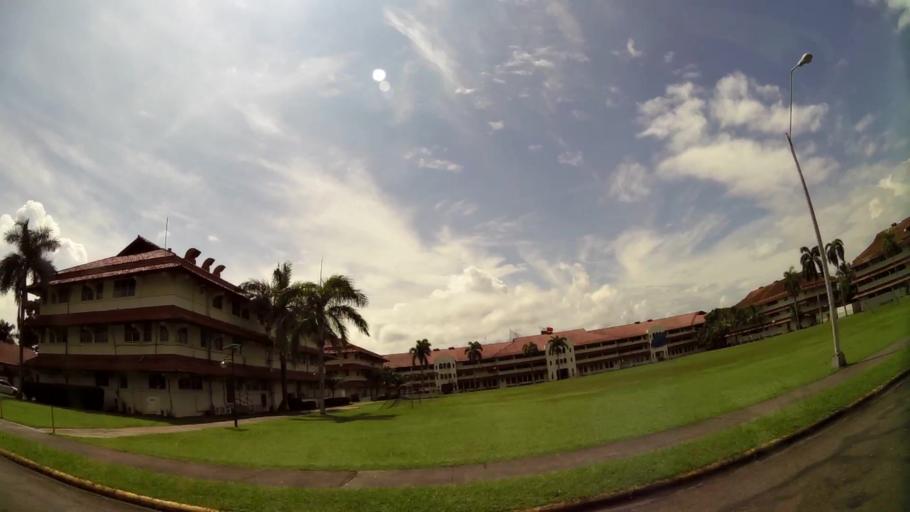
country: PA
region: Panama
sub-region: Distrito de Panama
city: Ancon
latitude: 8.9999
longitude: -79.5826
